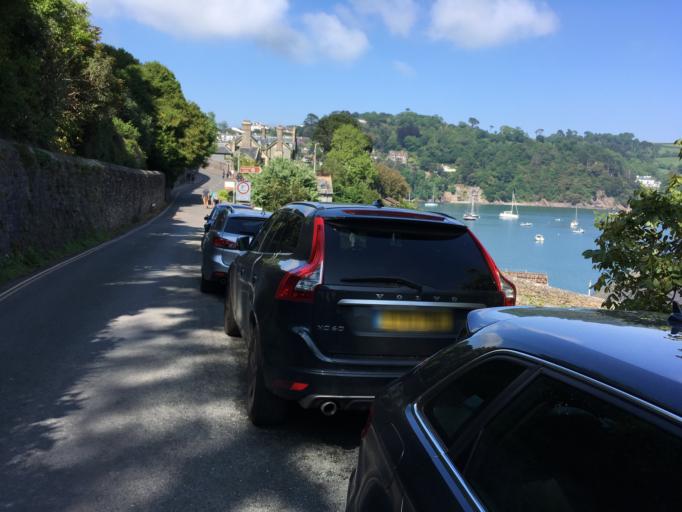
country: GB
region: England
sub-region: Devon
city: Dartmouth
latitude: 50.3425
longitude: -3.5742
